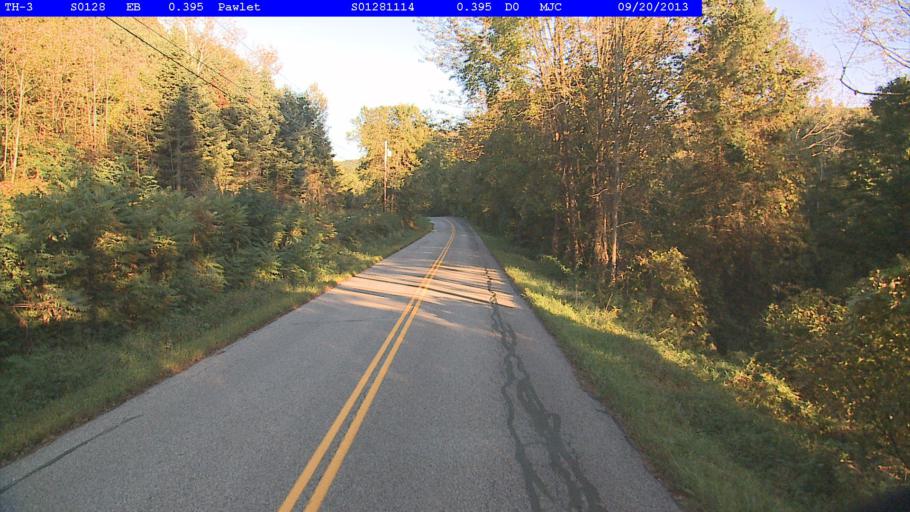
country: US
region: New York
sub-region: Washington County
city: Granville
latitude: 43.3716
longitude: -73.2224
